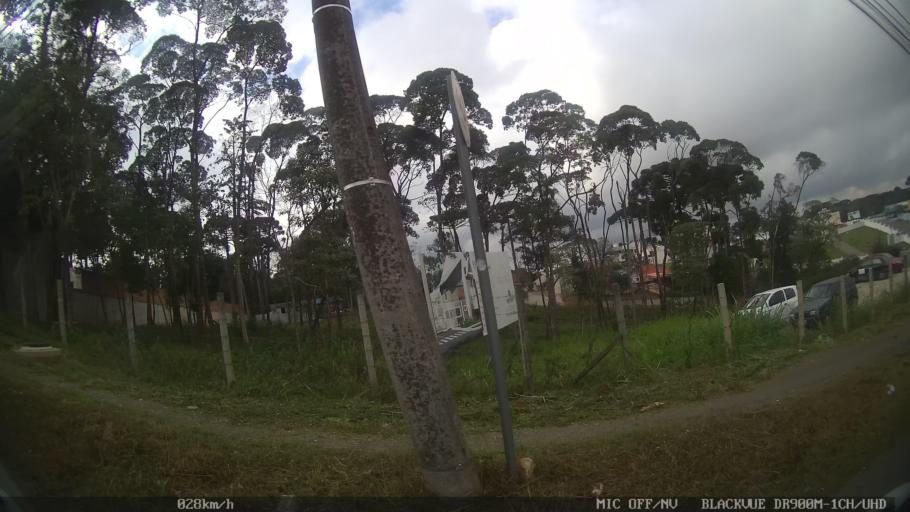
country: BR
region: Parana
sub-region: Curitiba
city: Curitiba
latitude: -25.3670
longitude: -49.2503
